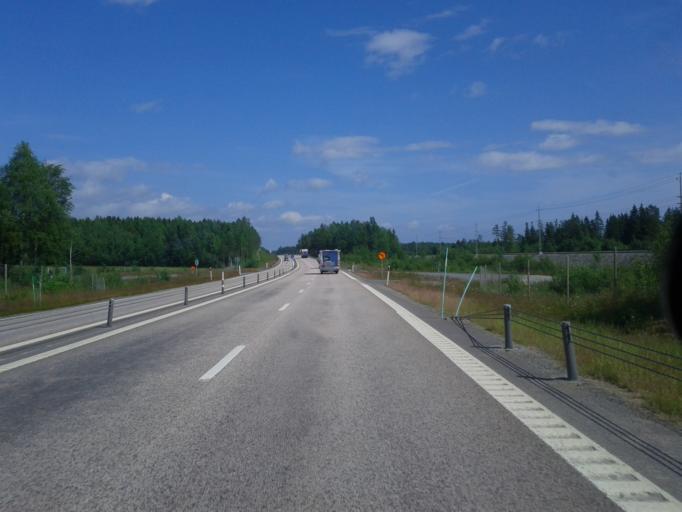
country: SE
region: Vaesterbotten
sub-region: Nordmalings Kommun
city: Nordmaling
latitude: 63.5041
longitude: 19.3442
